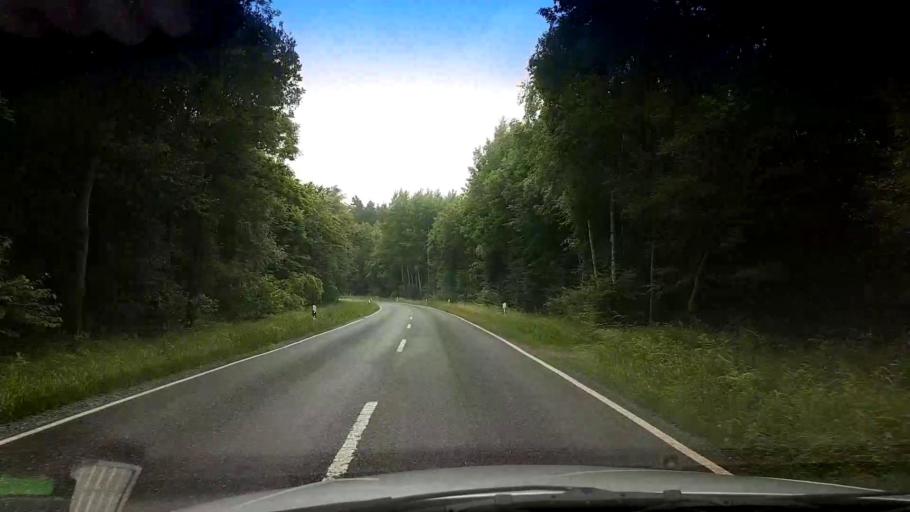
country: DE
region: Bavaria
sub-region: Upper Franconia
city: Weismain
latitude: 50.0850
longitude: 11.2927
